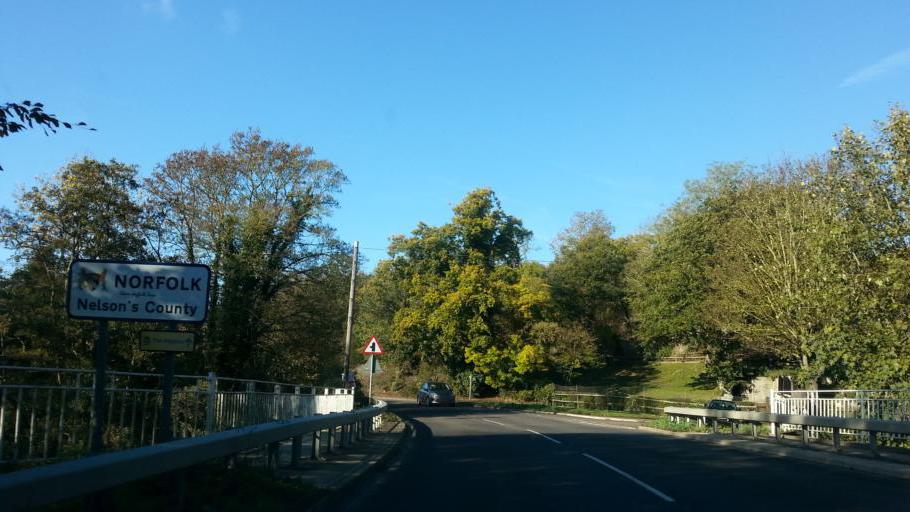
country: GB
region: England
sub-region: Norfolk
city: Harleston
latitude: 52.3916
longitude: 1.3004
